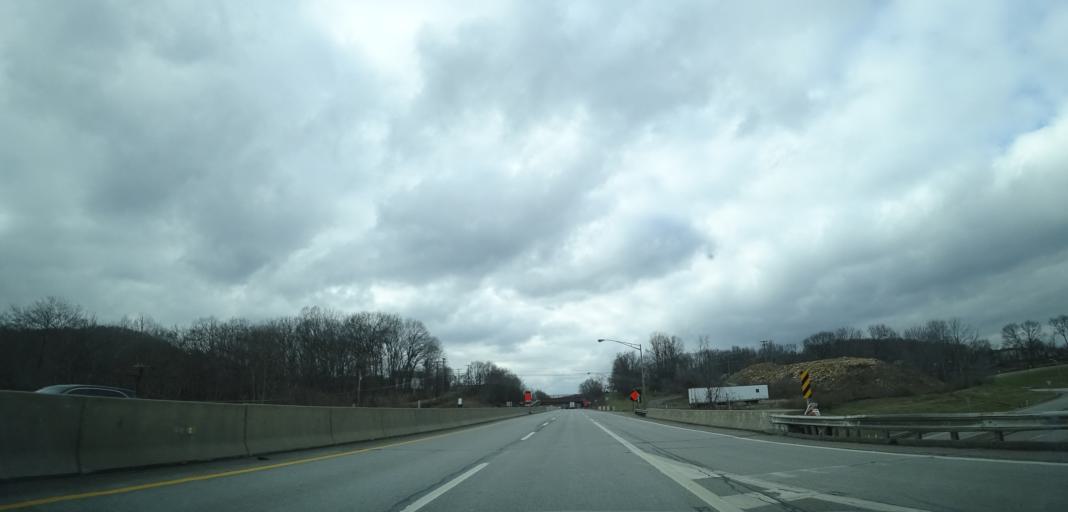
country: US
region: Pennsylvania
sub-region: Beaver County
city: West Mayfield
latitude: 40.8139
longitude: -80.3244
